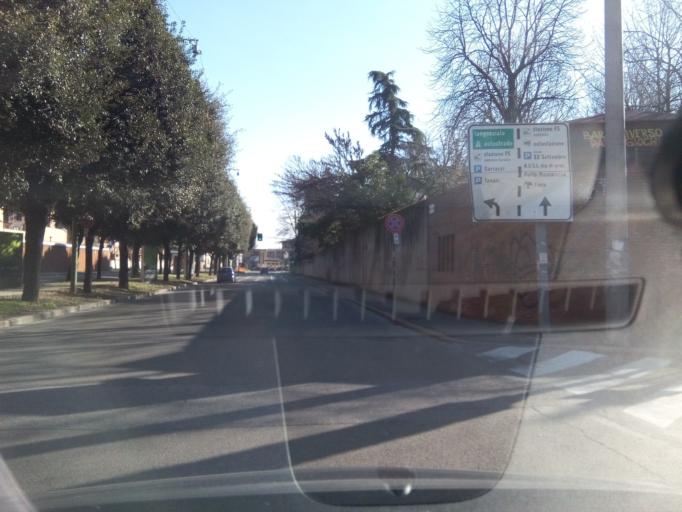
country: IT
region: Emilia-Romagna
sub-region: Provincia di Bologna
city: Bologna
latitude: 44.5042
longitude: 11.3365
